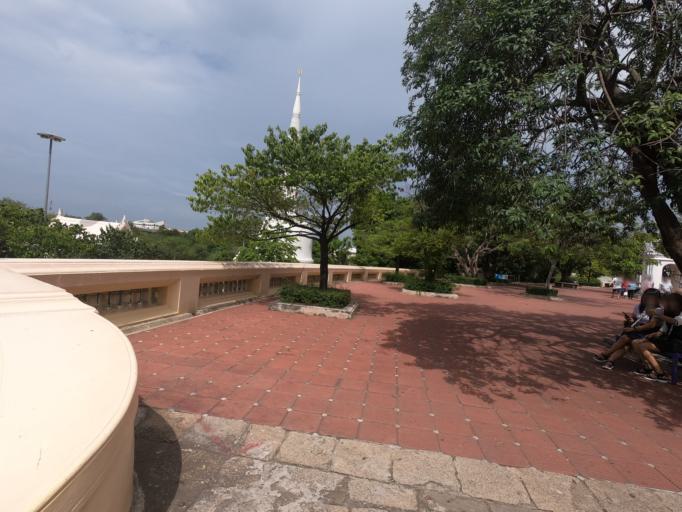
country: TH
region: Nakhon Pathom
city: Nakhon Pathom
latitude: 13.8189
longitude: 100.0602
